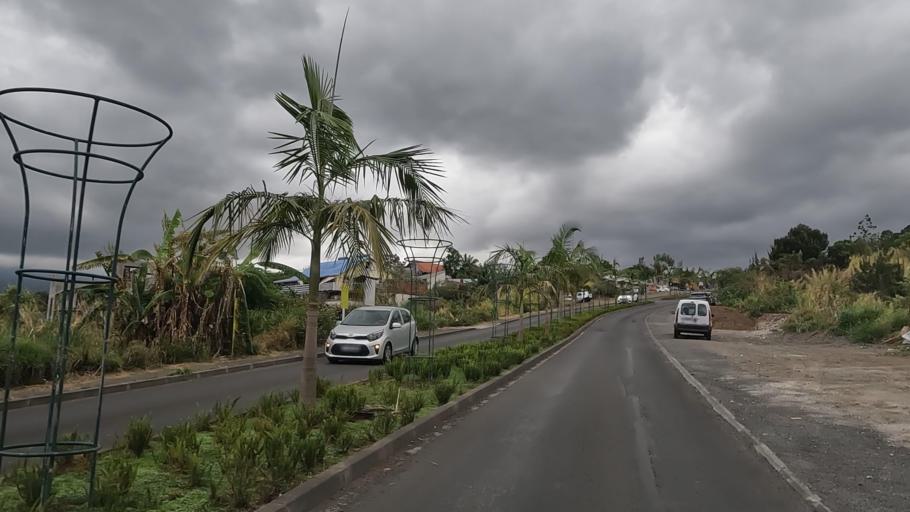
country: RE
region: Reunion
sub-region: Reunion
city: Le Tampon
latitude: -21.2656
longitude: 55.5124
